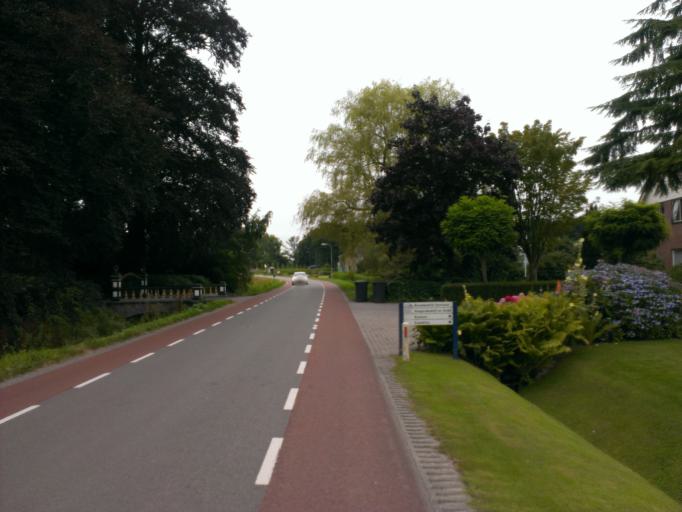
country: NL
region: Gelderland
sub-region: Gemeente Heerde
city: Heerde
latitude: 52.3769
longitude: 6.0498
